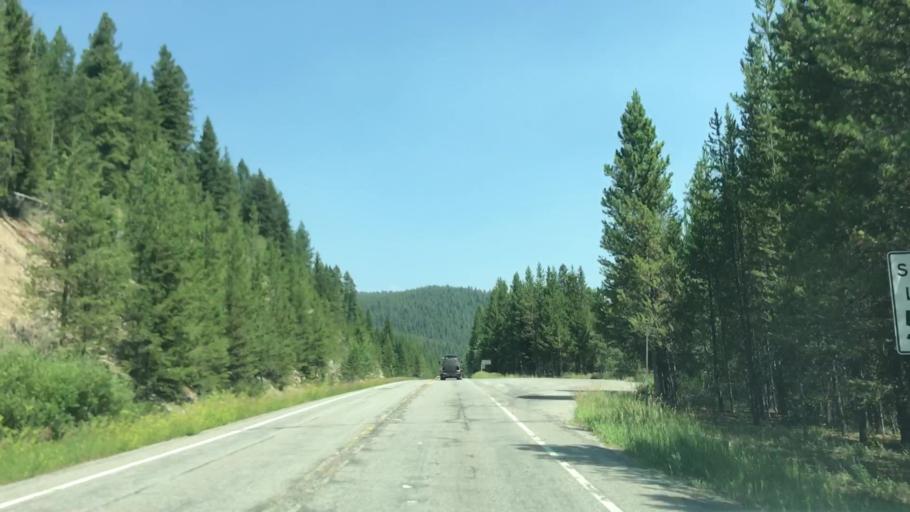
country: US
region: Montana
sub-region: Gallatin County
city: West Yellowstone
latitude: 44.8138
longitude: -111.0933
